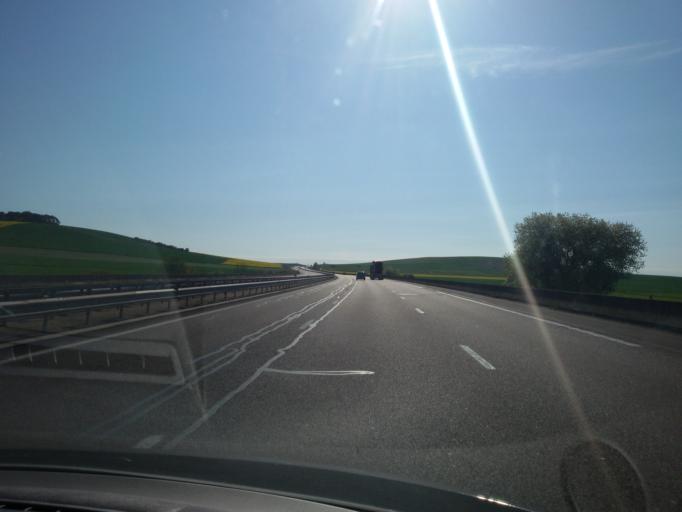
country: FR
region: Bourgogne
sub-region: Departement de l'Yonne
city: Aillant-sur-Tholon
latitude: 47.8982
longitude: 3.3651
